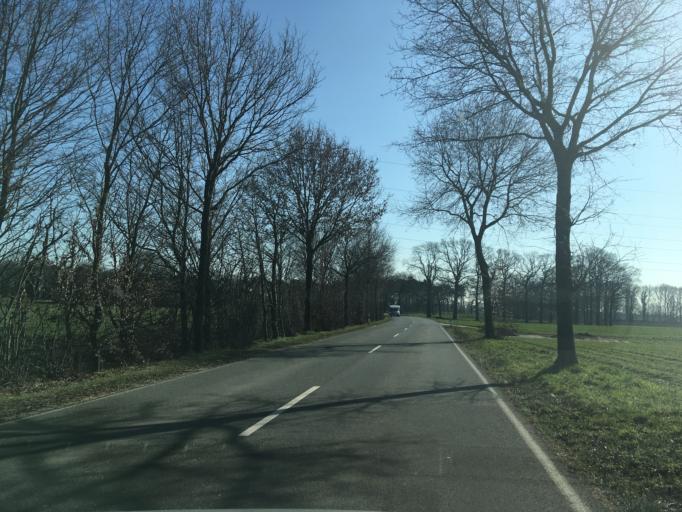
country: DE
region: North Rhine-Westphalia
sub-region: Regierungsbezirk Dusseldorf
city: Bocholt
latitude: 51.7962
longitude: 6.5812
